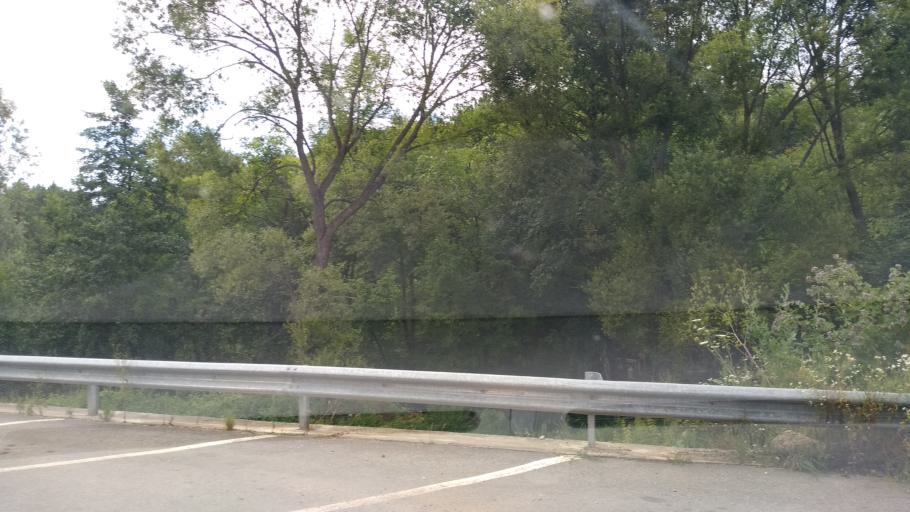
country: RO
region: Hunedoara
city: Salasu de Sus
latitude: 45.4852
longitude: 22.9467
